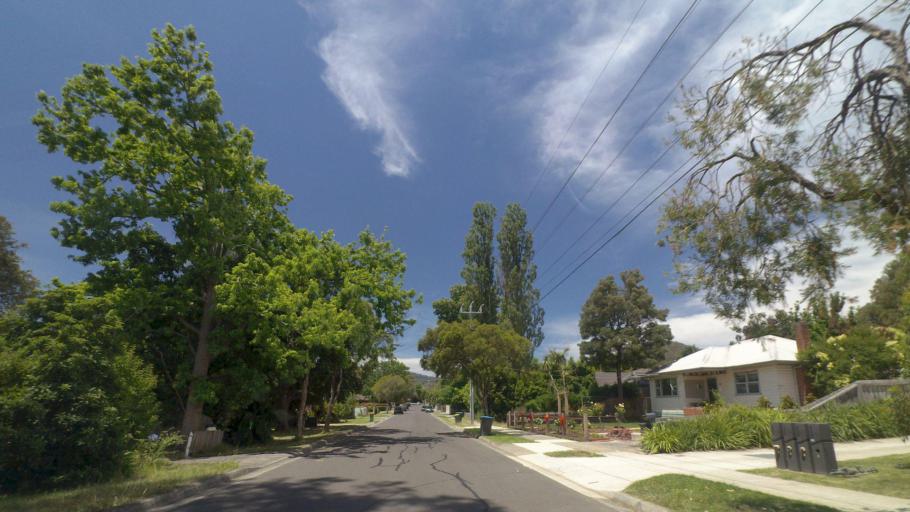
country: AU
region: Victoria
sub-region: Knox
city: Boronia
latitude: -37.8575
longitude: 145.2919
